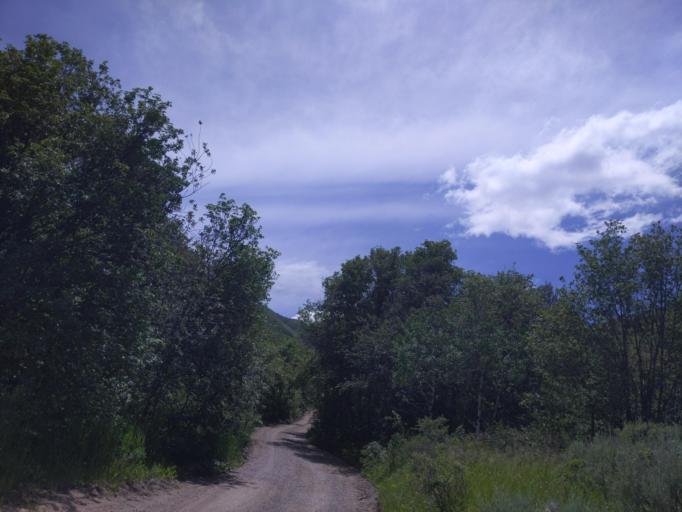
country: US
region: Idaho
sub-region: Bannock County
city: Pocatello
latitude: 42.8295
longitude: -112.4807
